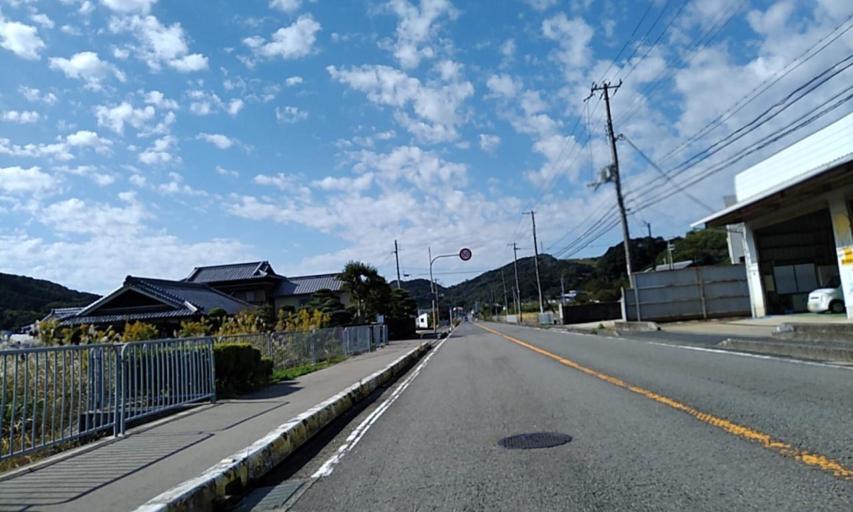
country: JP
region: Wakayama
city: Gobo
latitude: 33.9735
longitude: 135.1373
